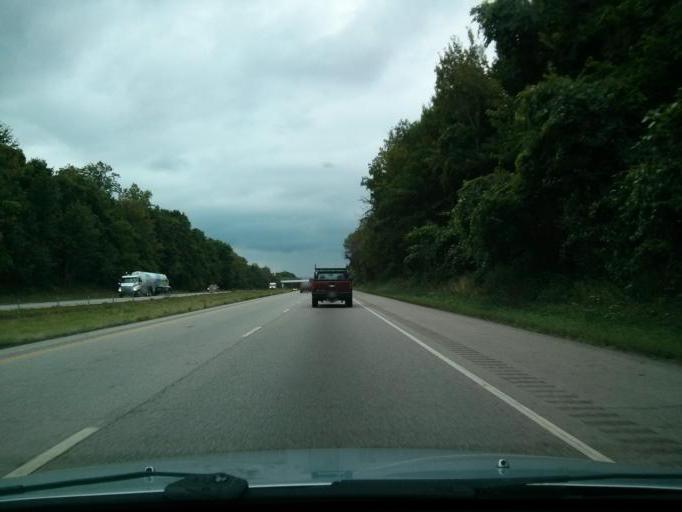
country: US
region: Ohio
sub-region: Mahoning County
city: Craig Beach
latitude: 41.1059
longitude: -81.0754
